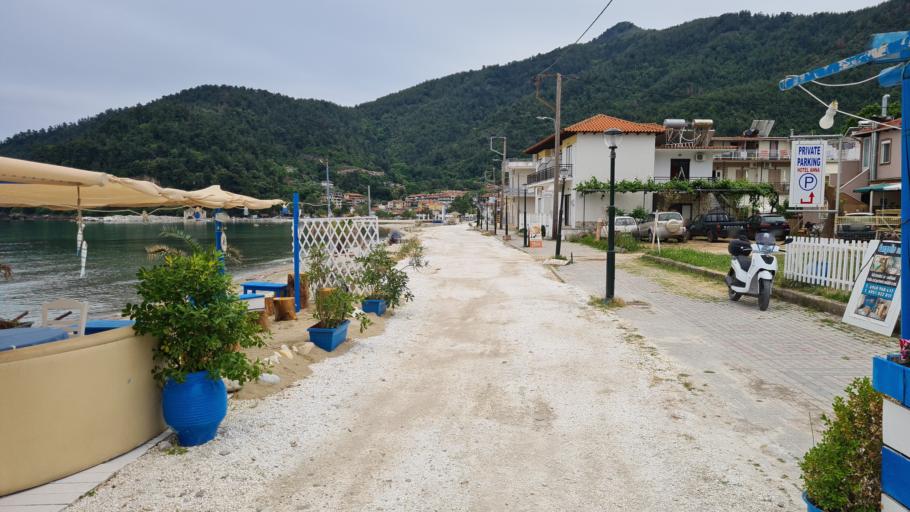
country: GR
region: East Macedonia and Thrace
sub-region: Nomos Kavalas
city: Potamia
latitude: 40.7131
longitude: 24.7581
